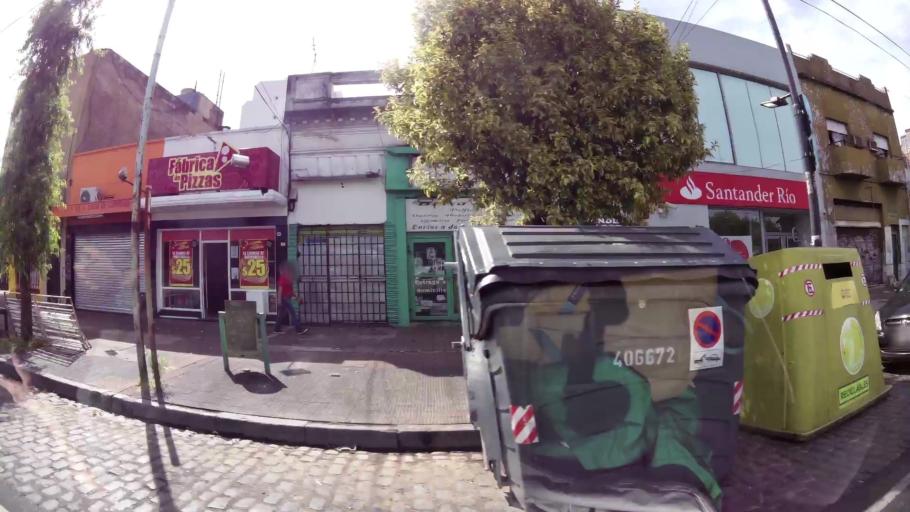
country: AR
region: Buenos Aires F.D.
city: Villa Lugano
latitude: -34.6553
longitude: -58.5070
